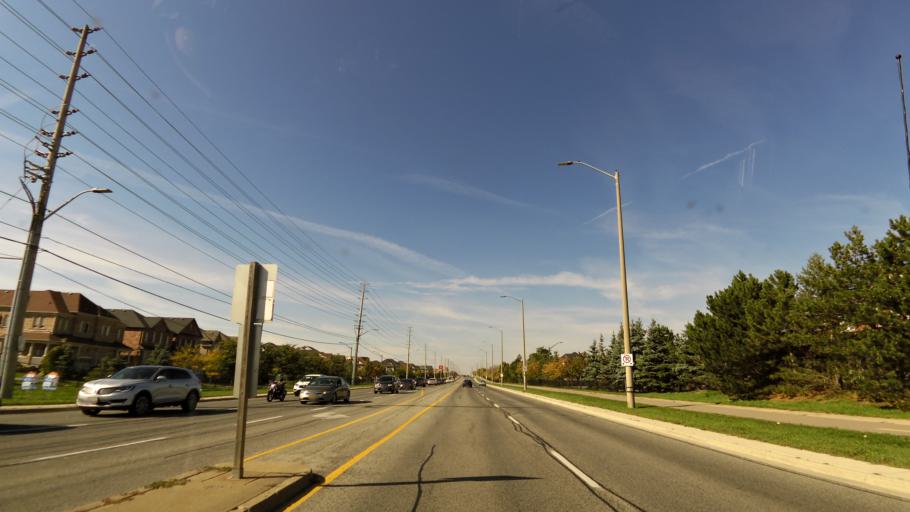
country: CA
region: Ontario
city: Mississauga
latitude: 43.5569
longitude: -79.7282
